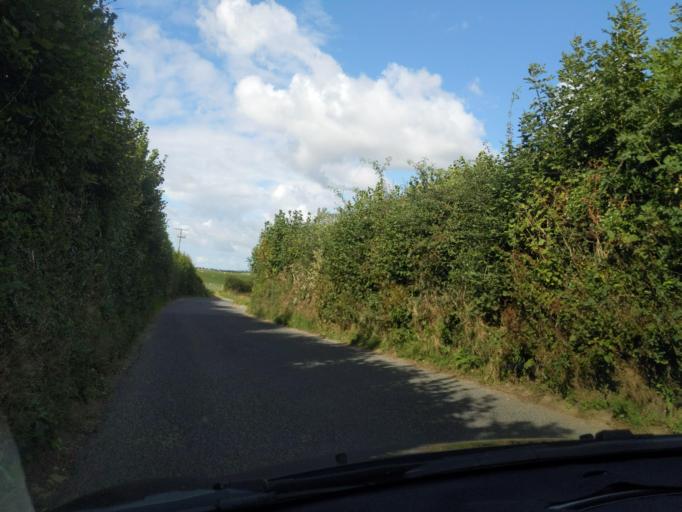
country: GB
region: England
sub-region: Devon
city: Great Torrington
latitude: 50.9231
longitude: -4.1978
